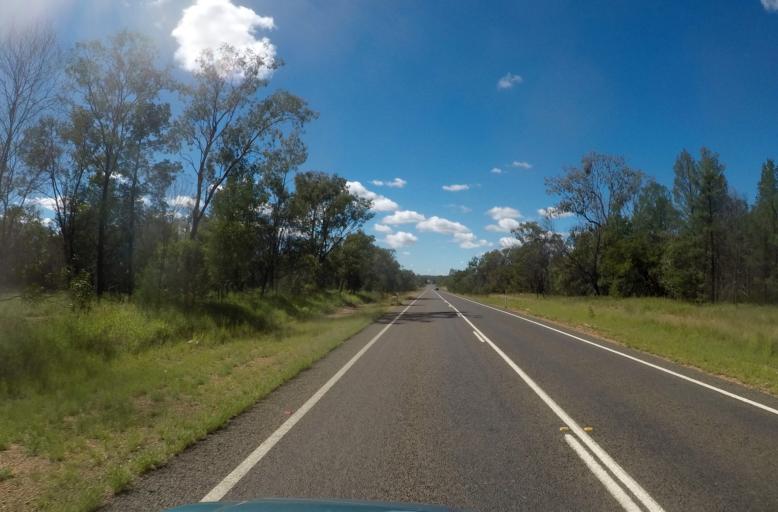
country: AU
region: Queensland
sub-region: Maranoa
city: Roma
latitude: -26.6185
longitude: 149.4276
